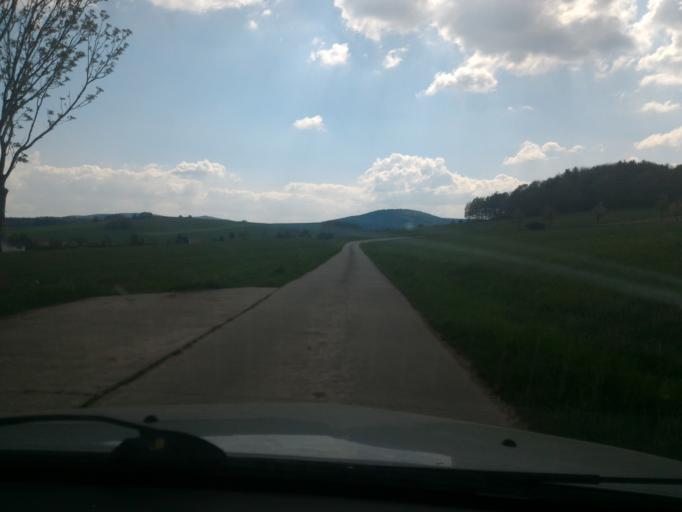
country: DE
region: Saxony
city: Kurort Jonsdorf
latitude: 50.8817
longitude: 14.7089
